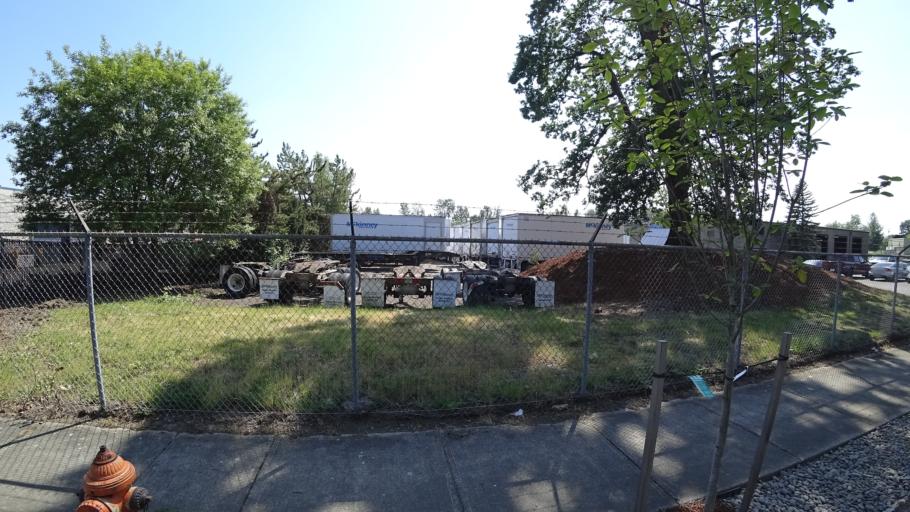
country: US
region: Oregon
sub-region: Multnomah County
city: Lents
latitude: 45.5634
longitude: -122.5383
